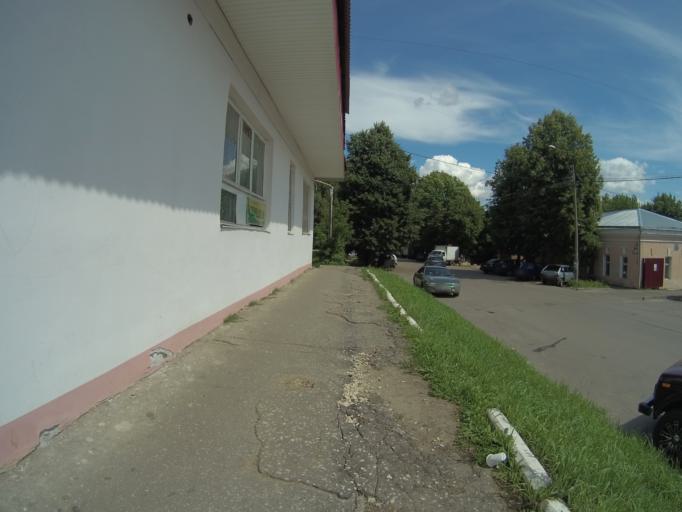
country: RU
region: Vladimir
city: Vladimir
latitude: 56.1383
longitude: 40.4096
